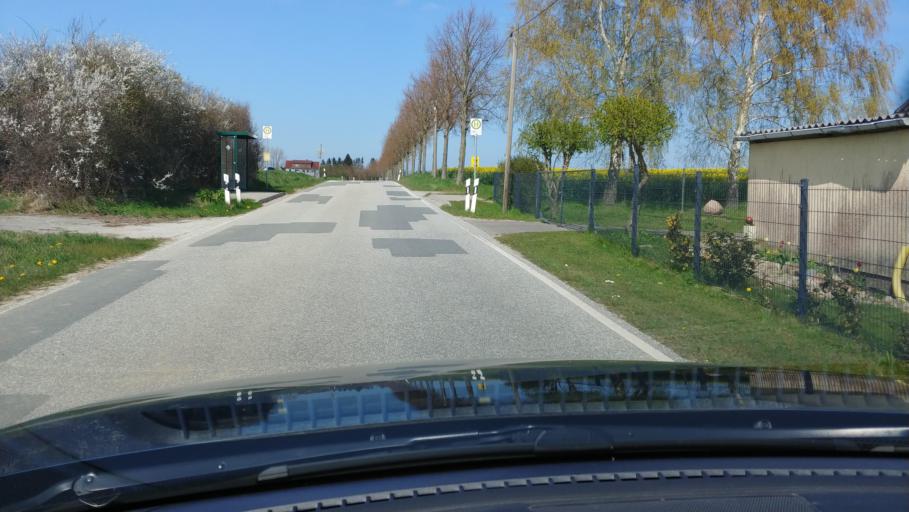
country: DE
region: Mecklenburg-Vorpommern
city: Muhlen Eichsen
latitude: 53.7977
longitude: 11.2661
